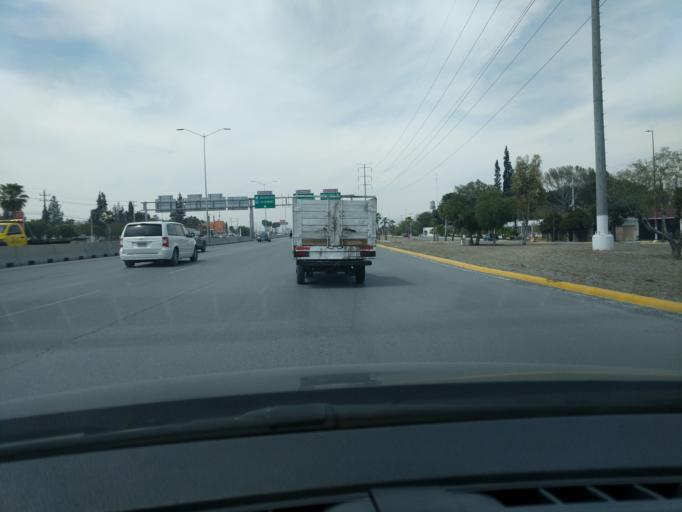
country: MX
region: Coahuila
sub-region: Arteaga
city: Arteaga
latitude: 25.4349
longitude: -100.9180
